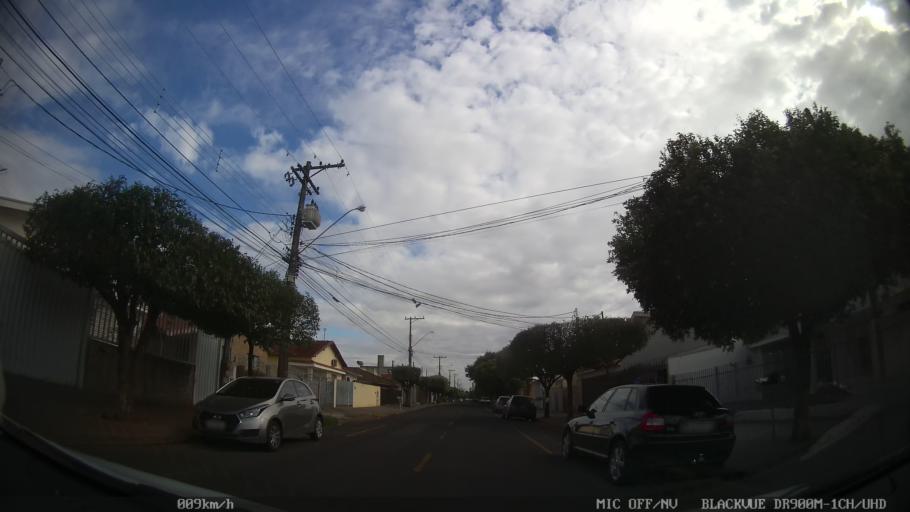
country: BR
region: Sao Paulo
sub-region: Sao Jose Do Rio Preto
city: Sao Jose do Rio Preto
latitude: -20.8393
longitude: -49.3731
